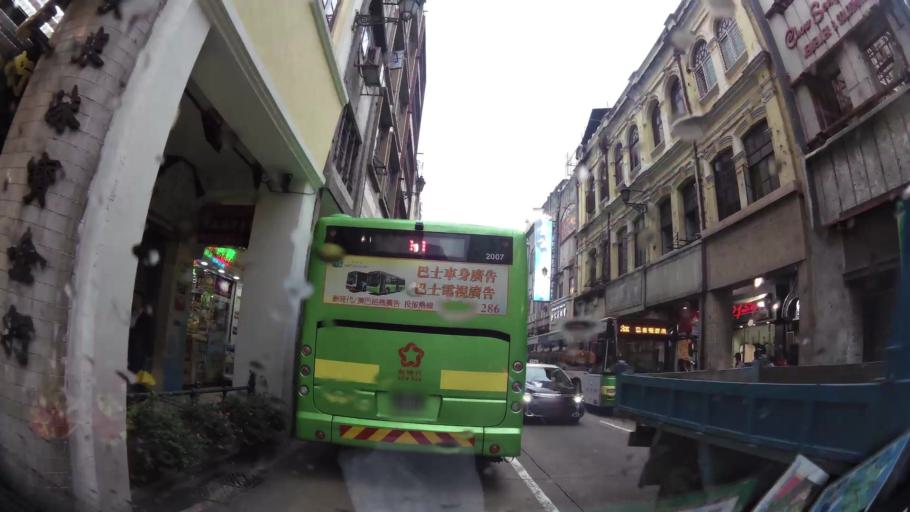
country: MO
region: Macau
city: Macau
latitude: 22.1946
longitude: 113.5384
